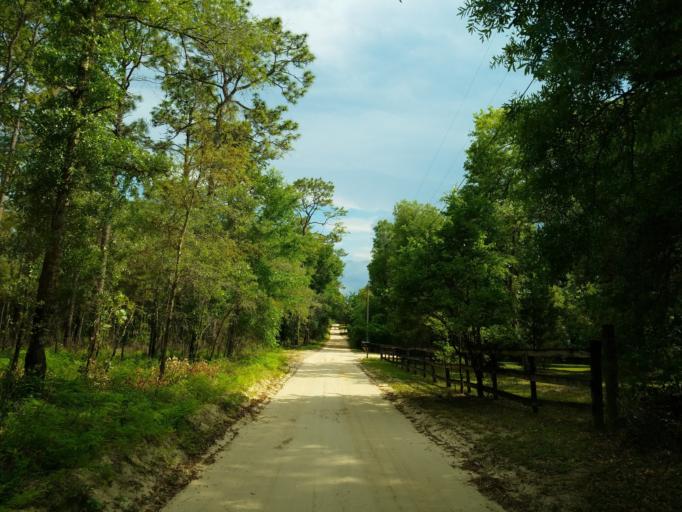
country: US
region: Florida
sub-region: Hernando County
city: Hill 'n Dale
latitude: 28.5565
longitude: -82.2802
